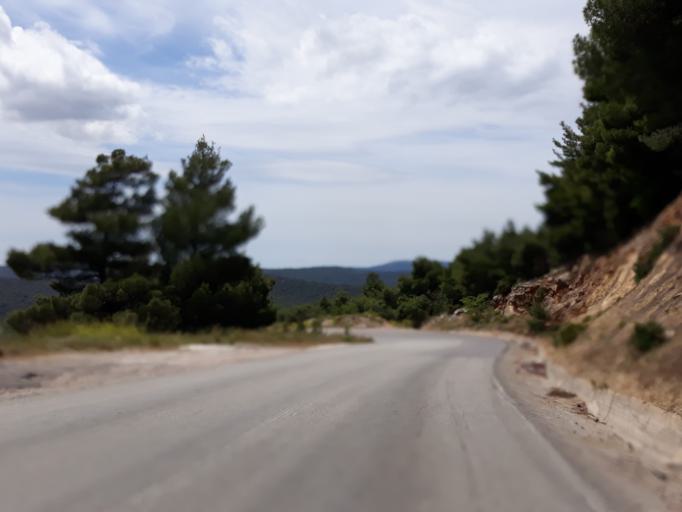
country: GR
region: Attica
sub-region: Nomarchia Dytikis Attikis
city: Magoula
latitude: 38.1525
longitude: 23.5169
